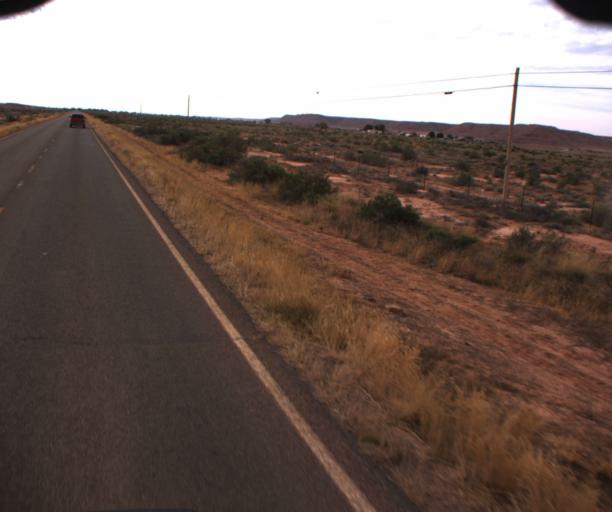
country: US
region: Arizona
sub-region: Apache County
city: Many Farms
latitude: 36.2972
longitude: -109.6065
